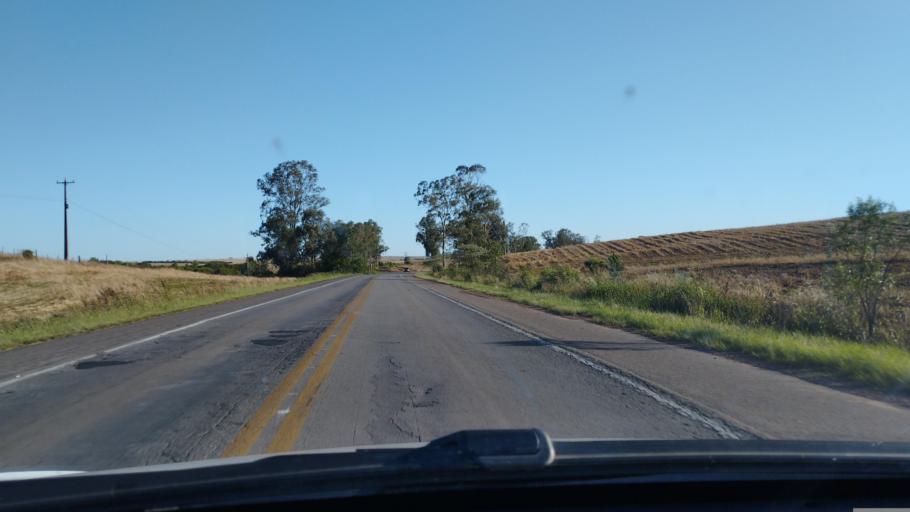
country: BR
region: Rio Grande do Sul
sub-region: Julio De Castilhos
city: Julio de Castilhos
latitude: -29.4066
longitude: -53.6680
